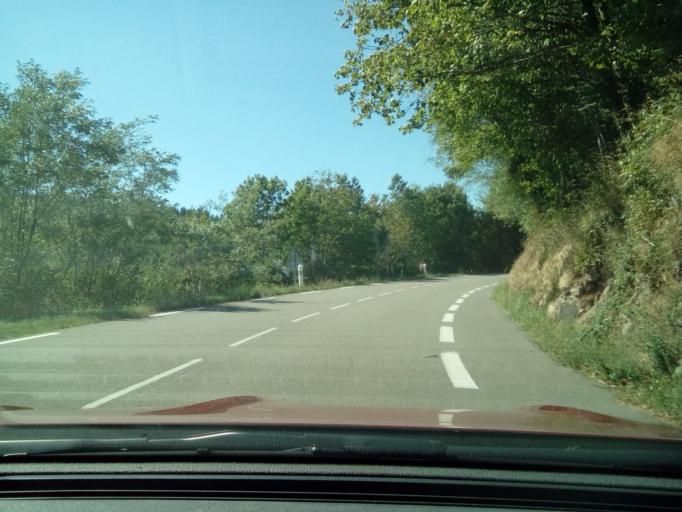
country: FR
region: Rhone-Alpes
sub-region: Departement du Rhone
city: Cublize
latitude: 45.9713
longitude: 4.4040
